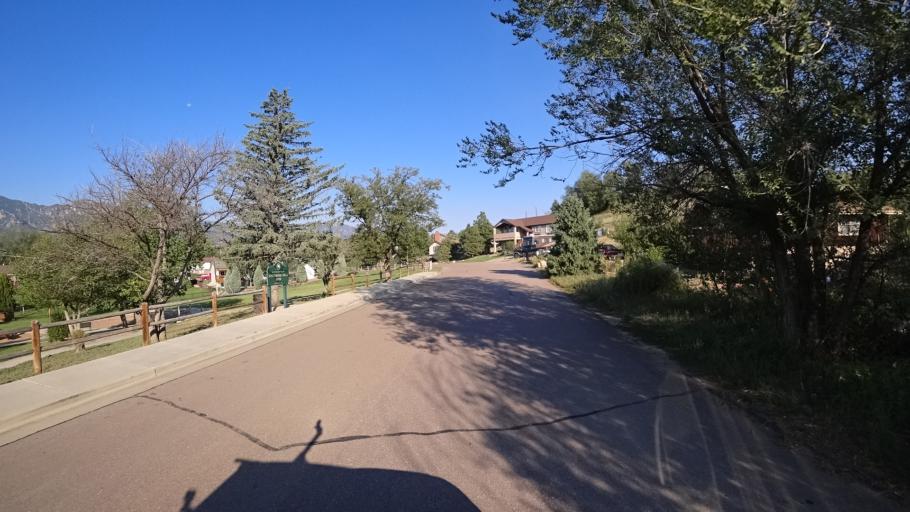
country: US
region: Colorado
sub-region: El Paso County
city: Stratmoor
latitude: 38.7779
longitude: -104.7921
